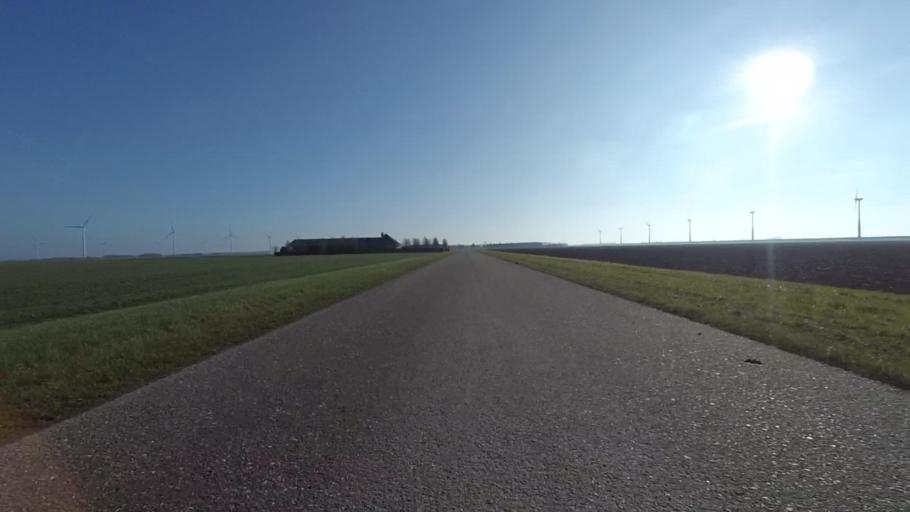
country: NL
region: Utrecht
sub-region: Gemeente Bunschoten
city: Spakenburg
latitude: 52.2854
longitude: 5.3634
